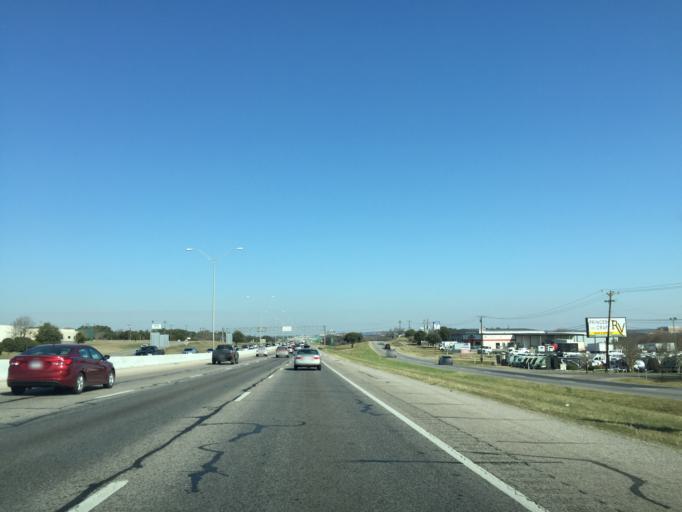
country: US
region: Texas
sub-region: Williamson County
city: Round Rock
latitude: 30.5430
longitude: -97.6922
